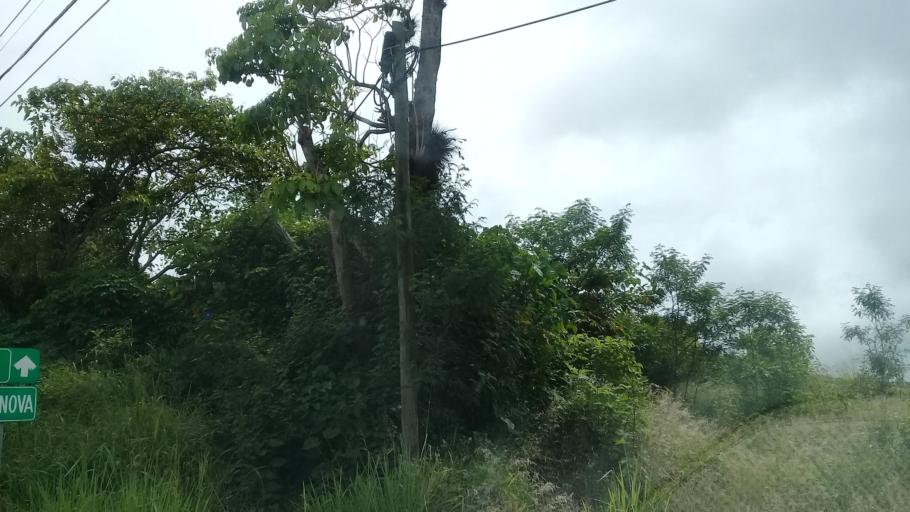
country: MX
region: Veracruz
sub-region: Emiliano Zapata
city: Jacarandas
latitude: 19.4848
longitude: -96.8575
